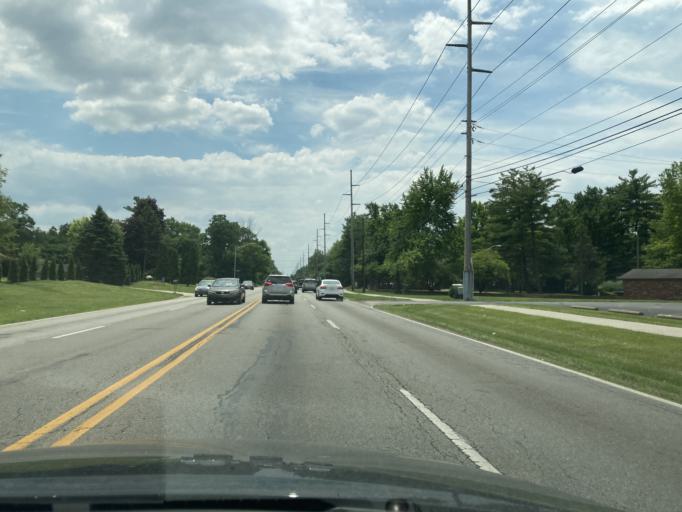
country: US
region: Indiana
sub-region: Marion County
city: Meridian Hills
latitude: 39.8521
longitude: -86.1941
